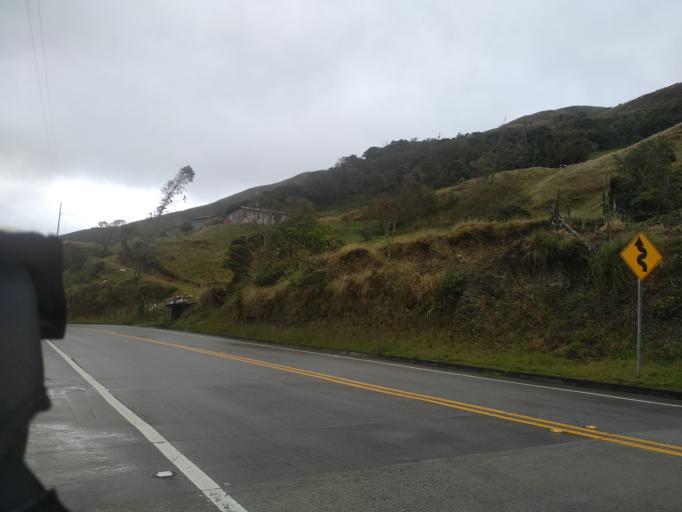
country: EC
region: Loja
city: Loja
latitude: -3.9025
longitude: -79.2570
